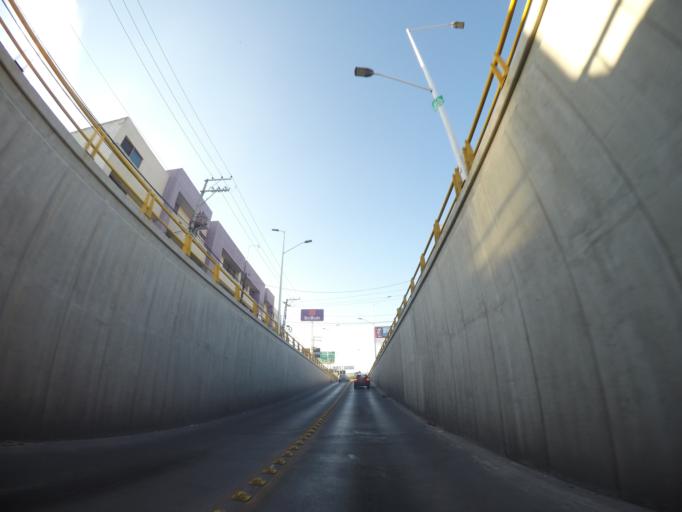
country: MX
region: San Luis Potosi
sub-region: San Luis Potosi
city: San Luis Potosi
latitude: 22.1659
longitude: -101.0012
